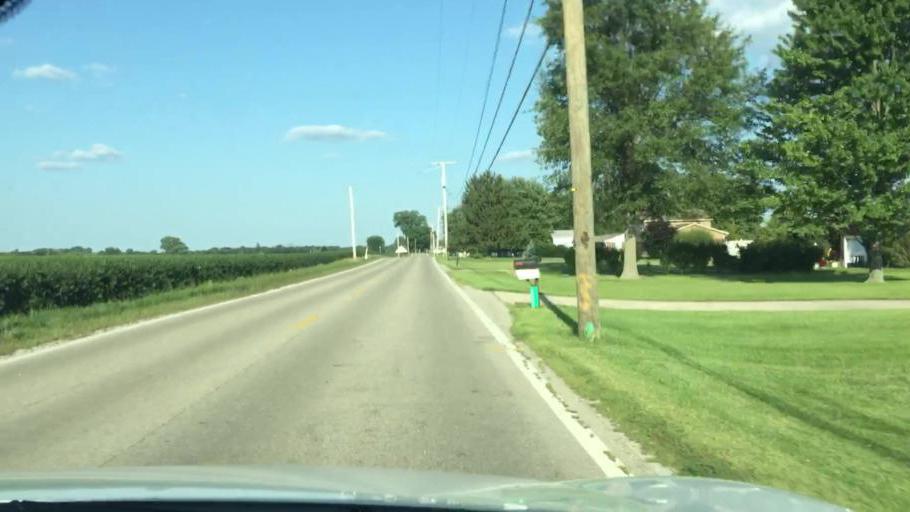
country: US
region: Ohio
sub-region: Clark County
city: Lisbon
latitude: 39.9411
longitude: -83.6907
